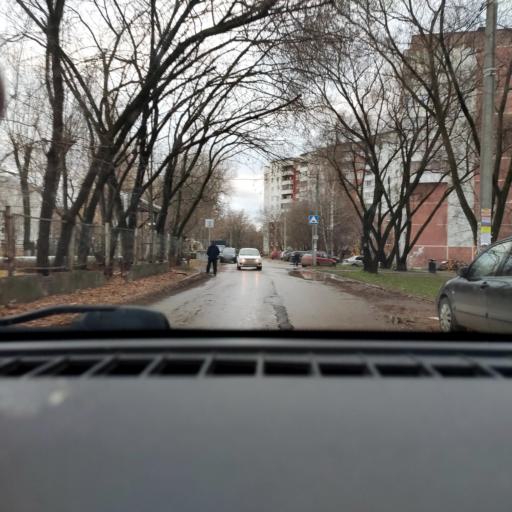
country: RU
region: Perm
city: Perm
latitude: 57.9770
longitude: 56.2756
